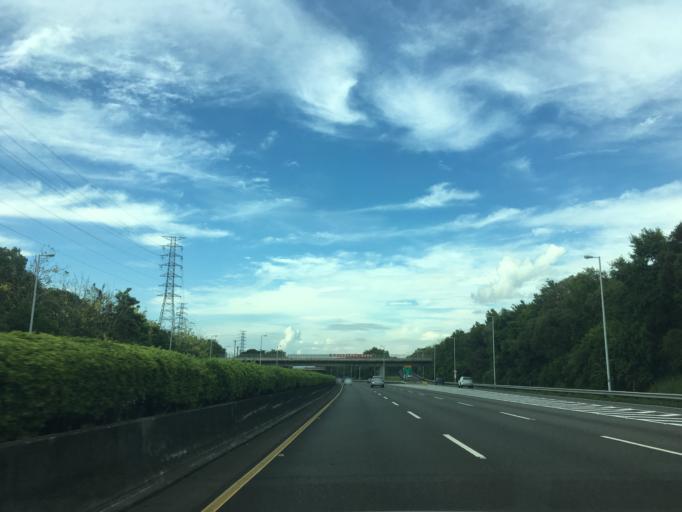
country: TW
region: Taiwan
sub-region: Yunlin
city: Douliu
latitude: 23.5907
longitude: 120.5199
